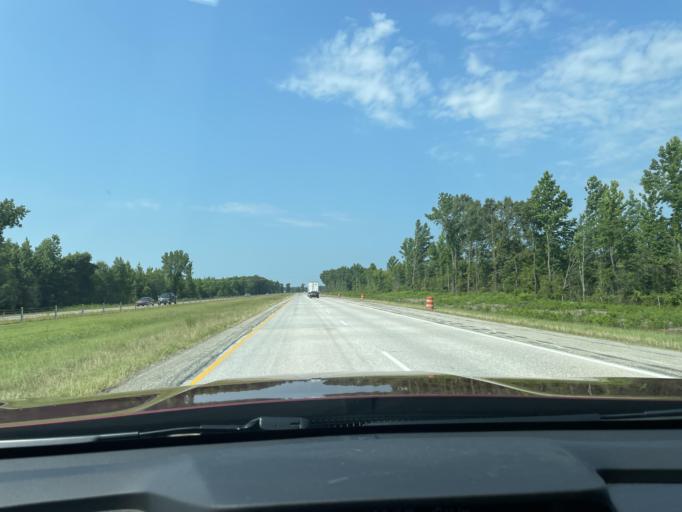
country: US
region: Arkansas
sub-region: White County
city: Searcy
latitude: 35.1571
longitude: -91.7853
